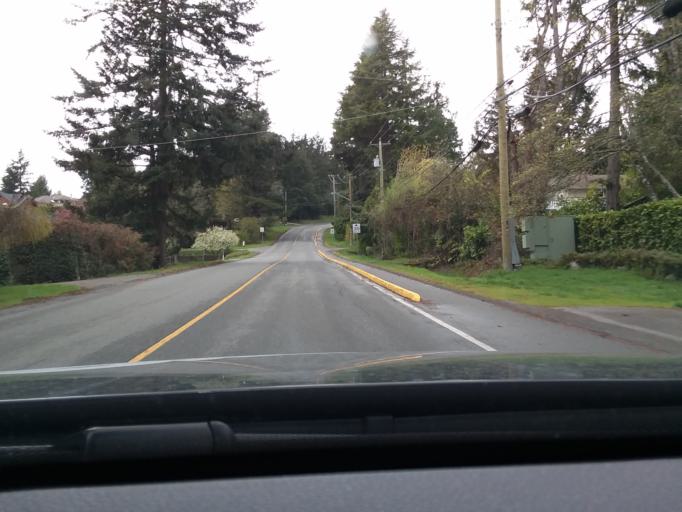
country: CA
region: British Columbia
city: North Saanich
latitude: 48.6176
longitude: -123.4220
